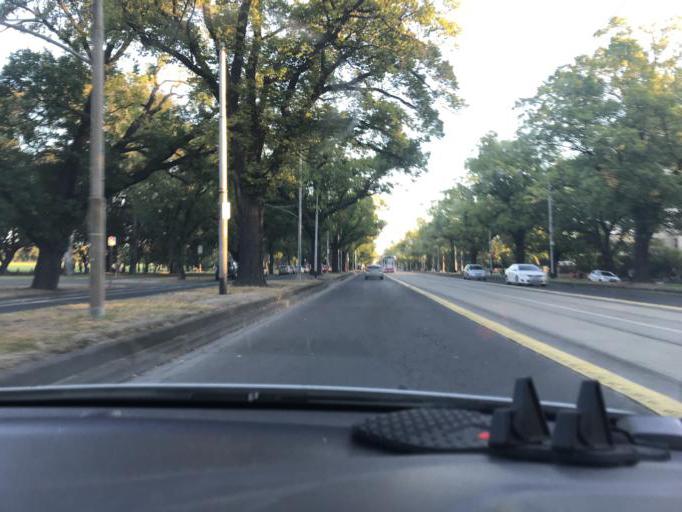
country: AU
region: Victoria
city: Carlton North
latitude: -37.7847
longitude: 144.9594
